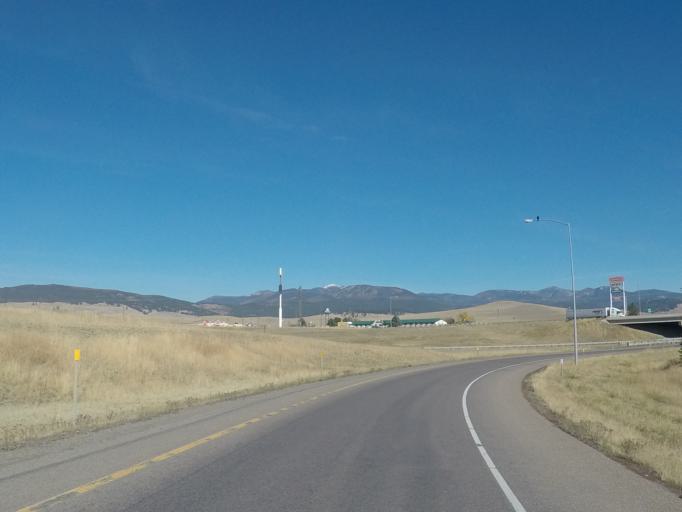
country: US
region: Montana
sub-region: Missoula County
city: Frenchtown
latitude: 46.9515
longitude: -114.1340
